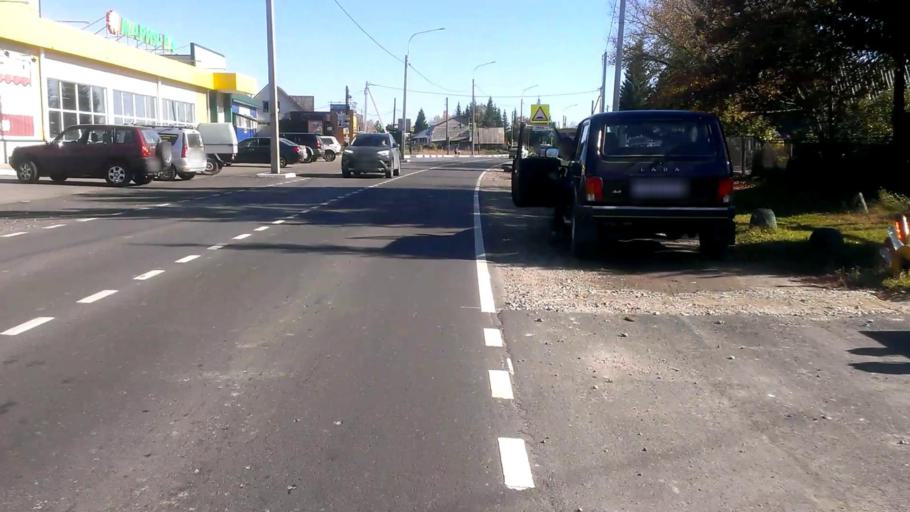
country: RU
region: Altai Krai
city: Sannikovo
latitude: 53.3171
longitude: 83.9550
